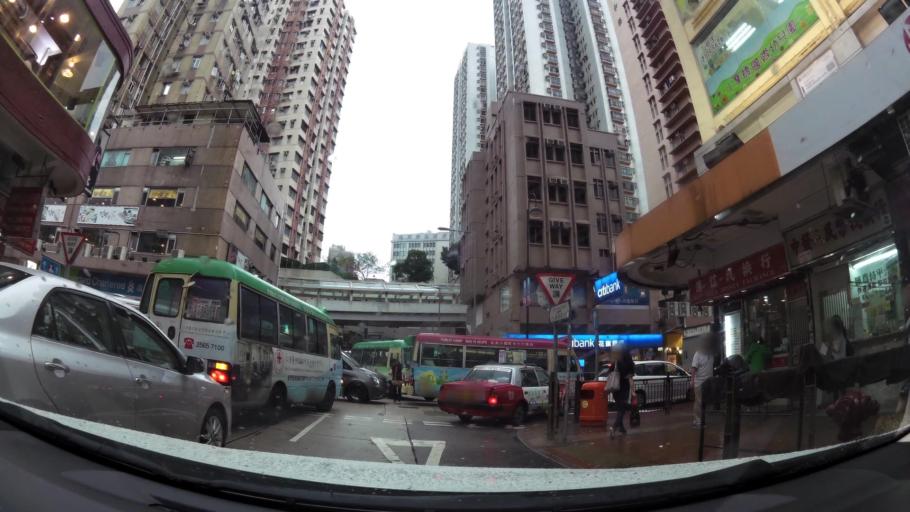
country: HK
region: Tsuen Wan
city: Tsuen Wan
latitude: 22.3720
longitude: 114.1178
